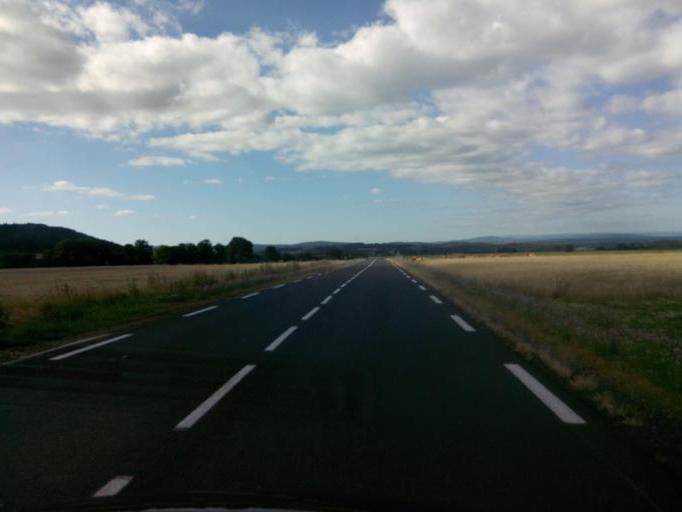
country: FR
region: Auvergne
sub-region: Departement de la Haute-Loire
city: Saint-Paulien
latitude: 45.1775
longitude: 3.8269
